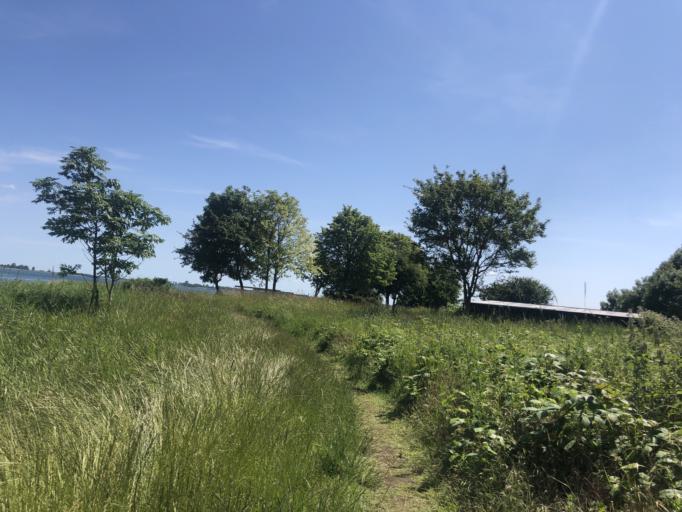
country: DK
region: South Denmark
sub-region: AEro Kommune
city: AEroskobing
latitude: 54.8858
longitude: 10.4159
